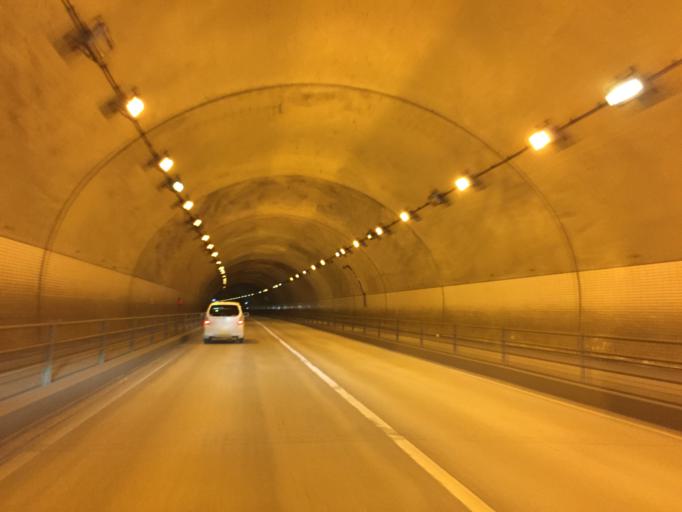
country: JP
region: Fukushima
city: Fukushima-shi
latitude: 37.7390
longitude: 140.4798
